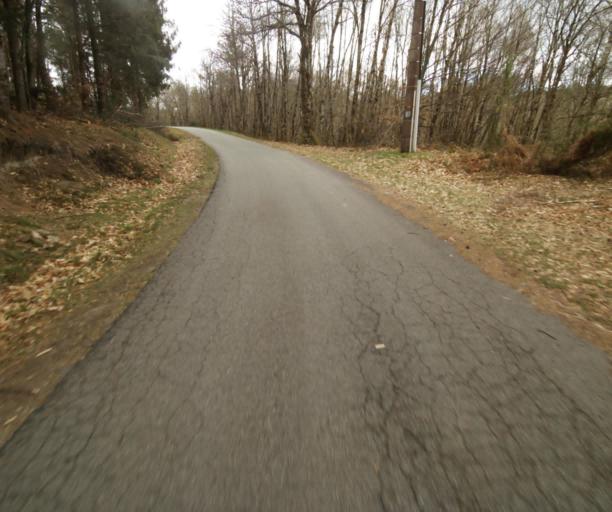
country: FR
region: Limousin
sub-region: Departement de la Correze
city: Correze
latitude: 45.3240
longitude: 1.9412
